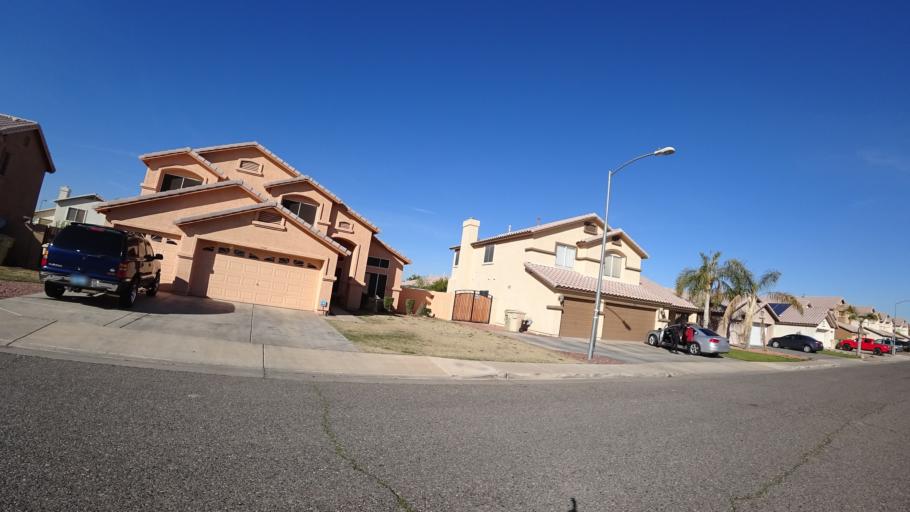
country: US
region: Arizona
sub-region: Maricopa County
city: Glendale
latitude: 33.5211
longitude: -112.2317
